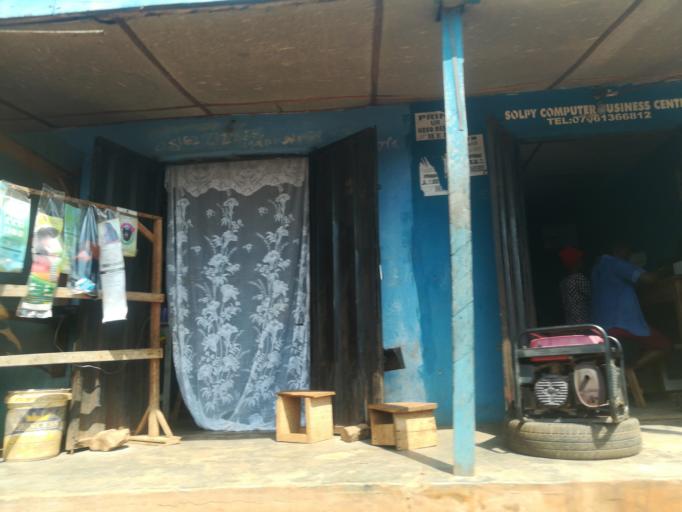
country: NG
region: Oyo
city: Moniya
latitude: 7.5231
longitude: 3.9135
